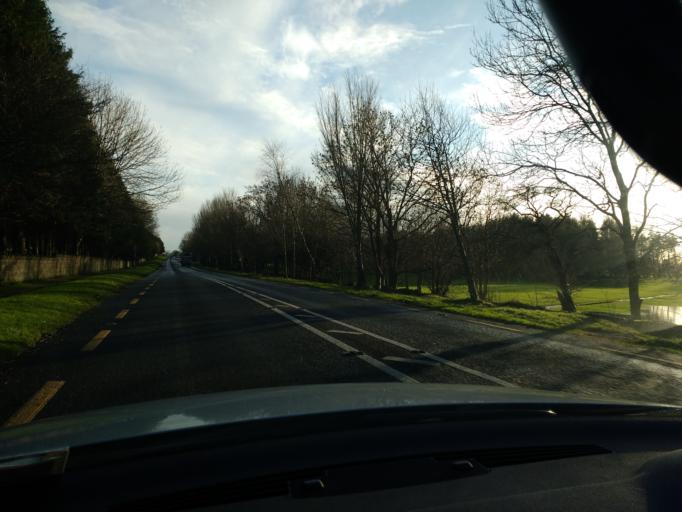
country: IE
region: Munster
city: Thurles
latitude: 52.6618
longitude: -7.8036
